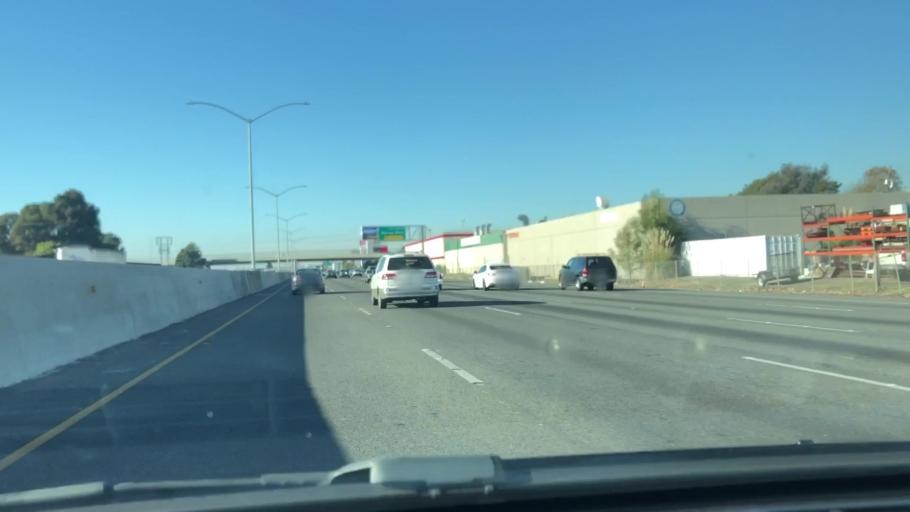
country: US
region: California
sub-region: Alameda County
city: San Leandro
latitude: 37.7046
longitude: -122.1580
